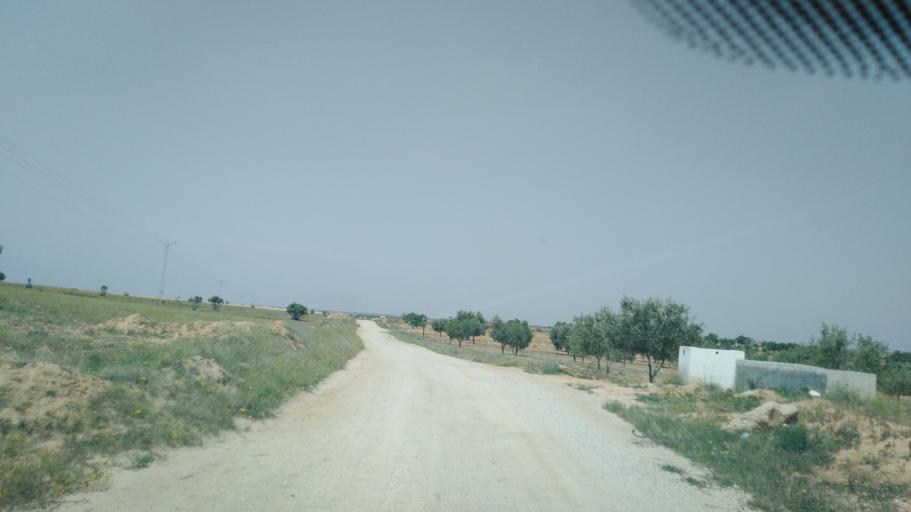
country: TN
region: Safaqis
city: Sfax
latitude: 34.7518
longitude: 10.5627
